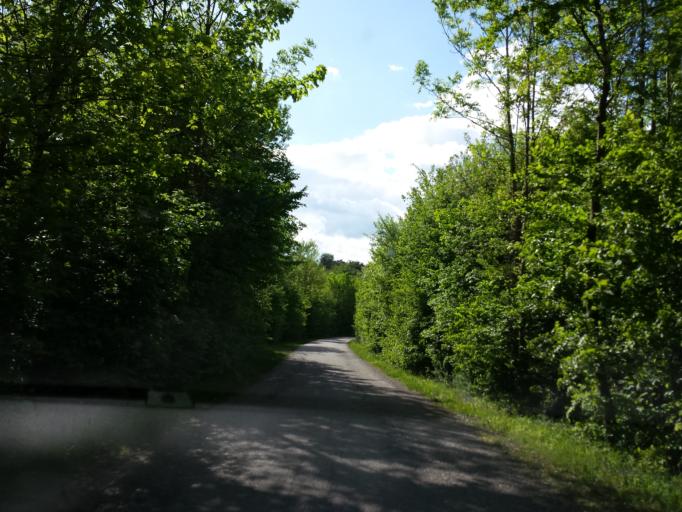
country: AT
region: Lower Austria
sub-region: Politischer Bezirk Baden
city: Hirtenberg
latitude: 47.9175
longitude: 16.1578
